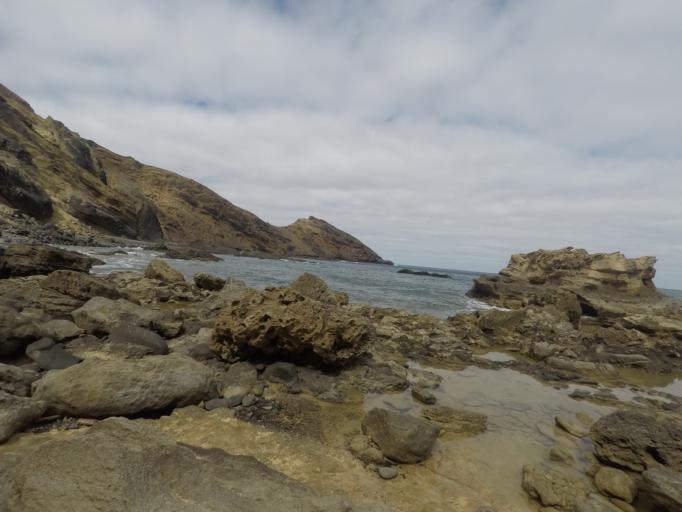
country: PT
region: Madeira
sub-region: Porto Santo
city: Vila de Porto Santo
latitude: 33.0742
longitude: -16.2950
